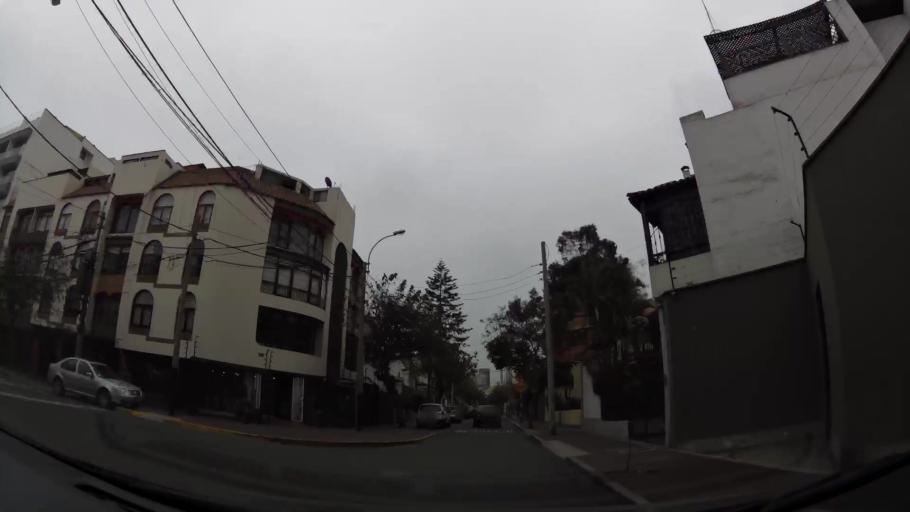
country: PE
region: Lima
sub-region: Lima
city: San Isidro
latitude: -12.1243
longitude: -77.0339
